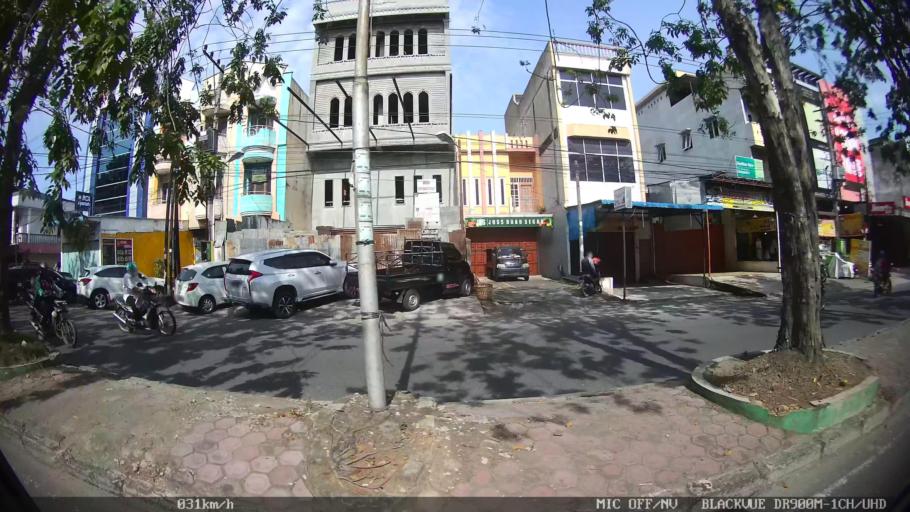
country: ID
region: North Sumatra
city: Medan
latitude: 3.5726
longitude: 98.6423
